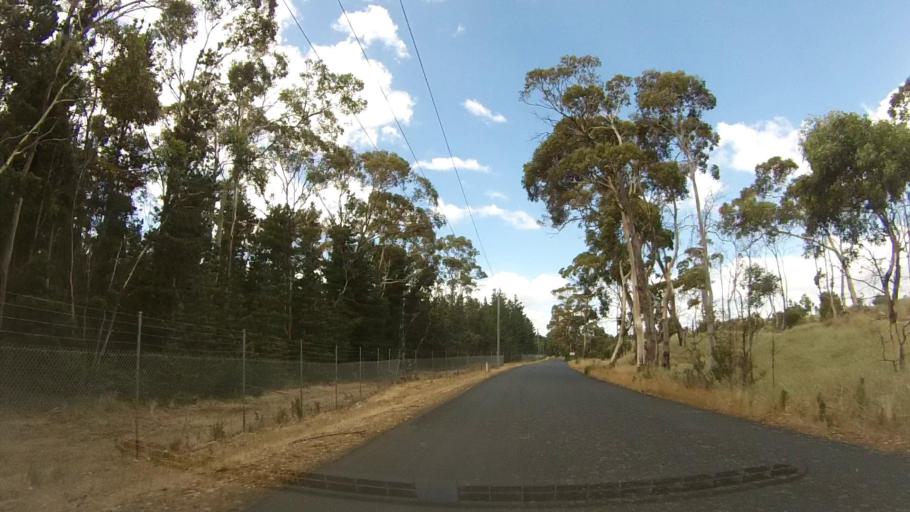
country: AU
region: Tasmania
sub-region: Clarence
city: Seven Mile Beach
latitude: -42.8445
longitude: 147.5303
